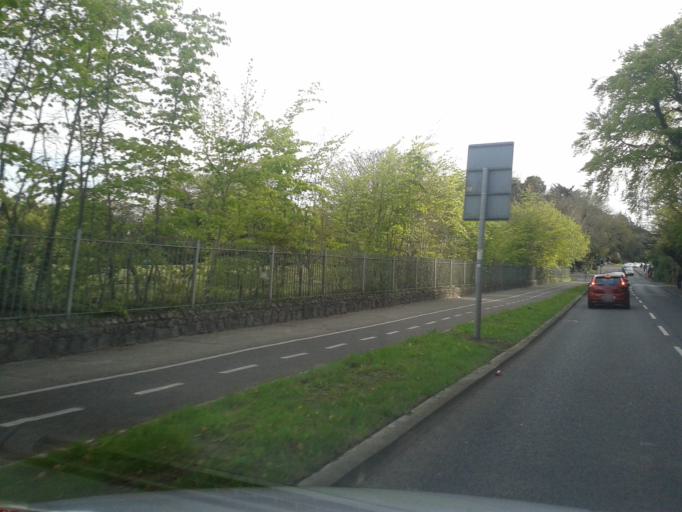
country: IE
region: Leinster
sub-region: Fingal County
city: Swords
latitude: 53.4510
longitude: -6.2305
